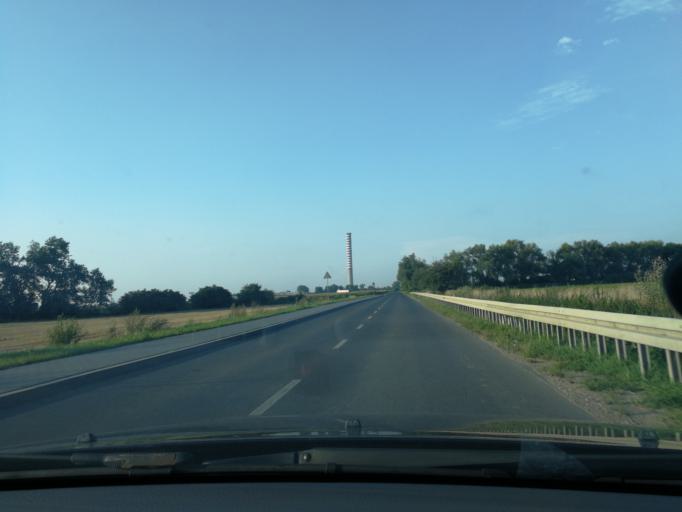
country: PL
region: Masovian Voivodeship
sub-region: Powiat pruszkowski
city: Brwinow
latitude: 52.1569
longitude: 20.7318
